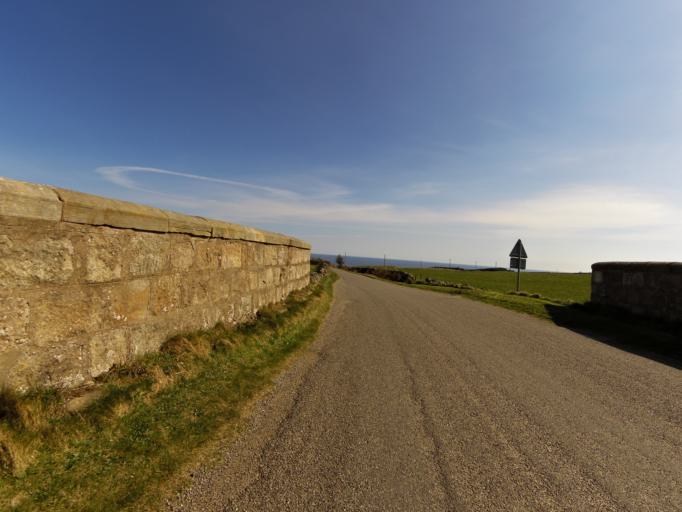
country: GB
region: Scotland
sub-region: Aberdeenshire
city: Portlethen
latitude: 57.0815
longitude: -2.1004
